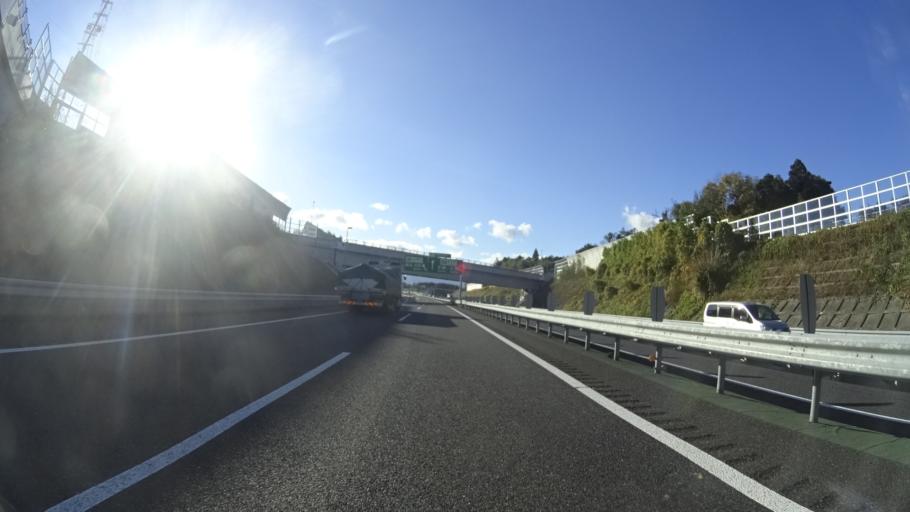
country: JP
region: Mie
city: Yokkaichi
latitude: 35.0490
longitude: 136.5925
